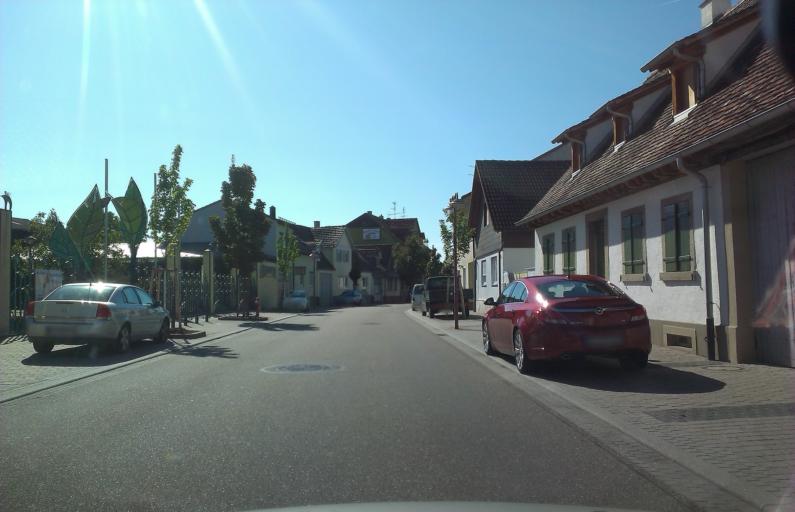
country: DE
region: Baden-Wuerttemberg
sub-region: Karlsruhe Region
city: Oberhausen-Rheinhausen
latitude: 49.2586
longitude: 8.4827
